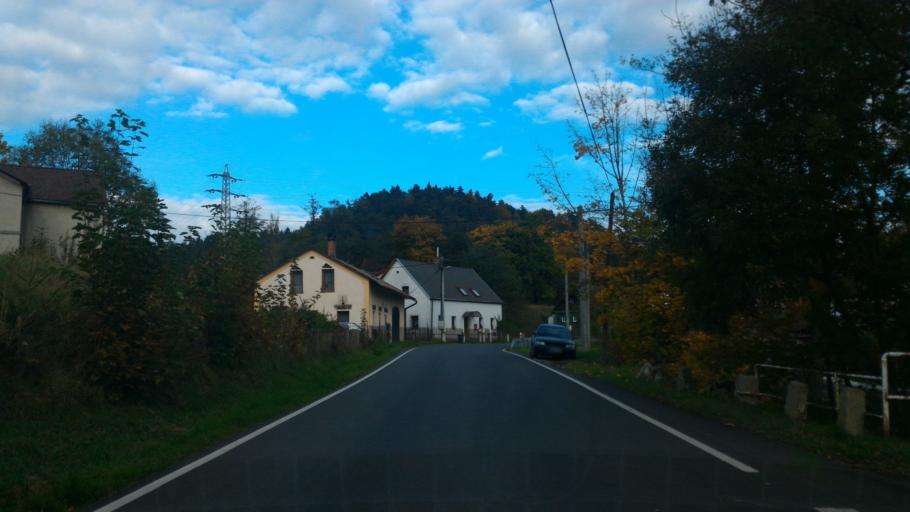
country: CZ
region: Ustecky
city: Ceska Kamenice
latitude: 50.8030
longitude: 14.4415
